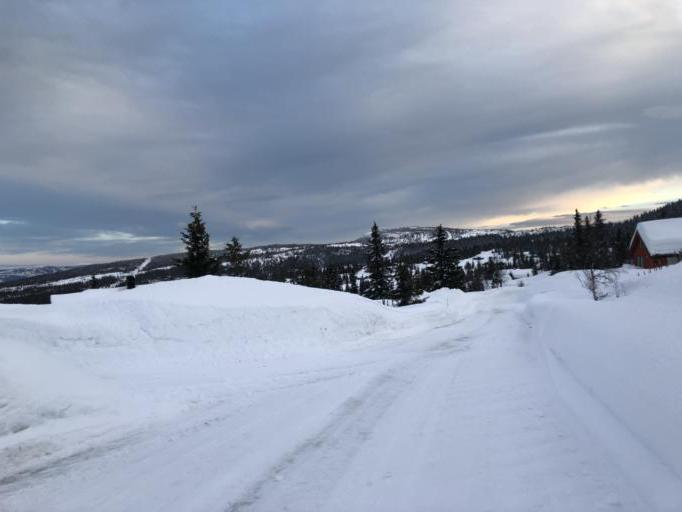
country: NO
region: Oppland
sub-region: Gausdal
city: Segalstad bru
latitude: 61.3300
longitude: 10.0528
